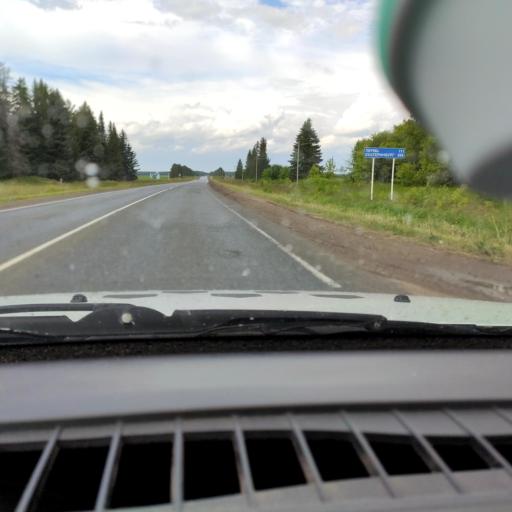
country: RU
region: Perm
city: Orda
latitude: 57.2035
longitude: 56.9227
